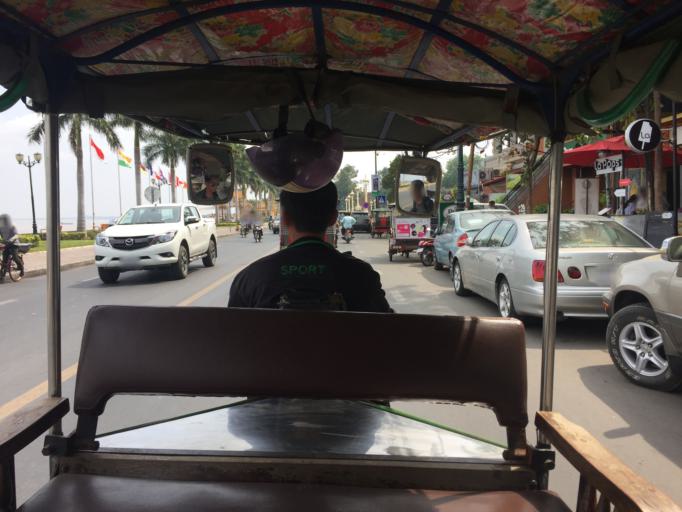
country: KH
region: Phnom Penh
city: Phnom Penh
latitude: 11.5665
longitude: 104.9319
